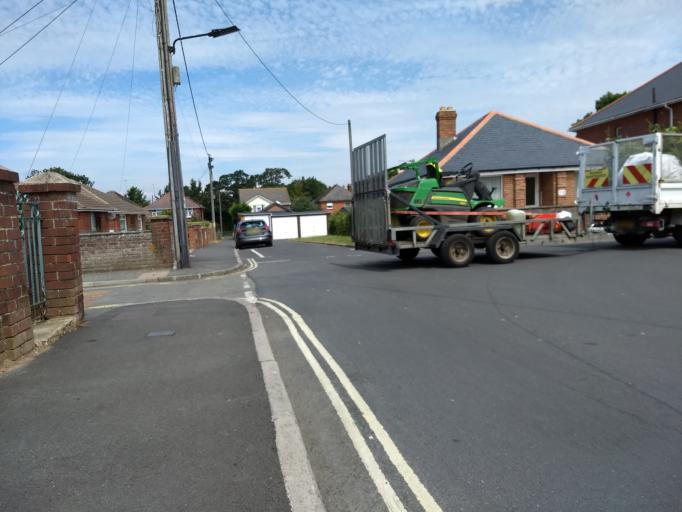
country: GB
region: England
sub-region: Isle of Wight
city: Newport
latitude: 50.7076
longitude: -1.3041
